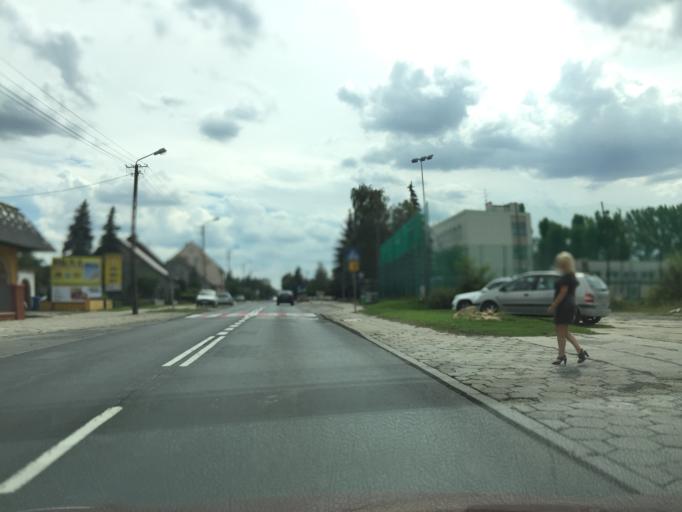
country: PL
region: Greater Poland Voivodeship
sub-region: Kalisz
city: Kalisz
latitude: 51.7431
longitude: 18.0963
